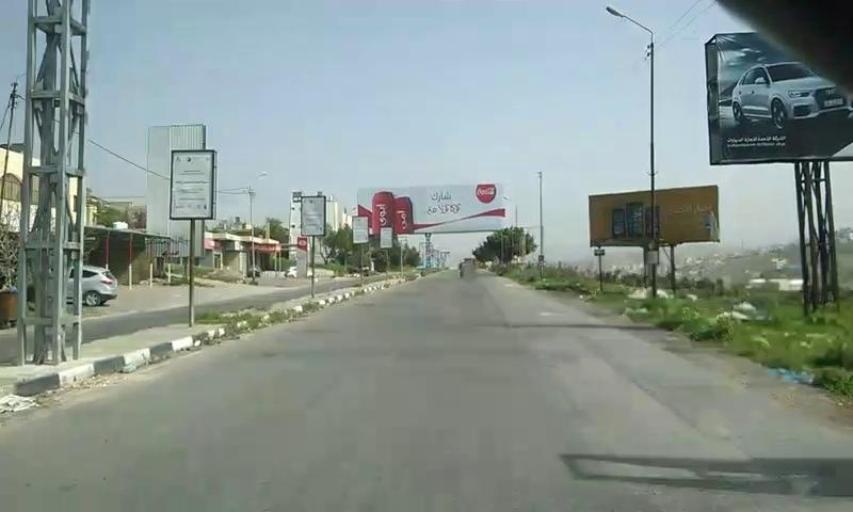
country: PS
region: West Bank
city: Kafr Qallil
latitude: 32.1836
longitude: 35.2776
